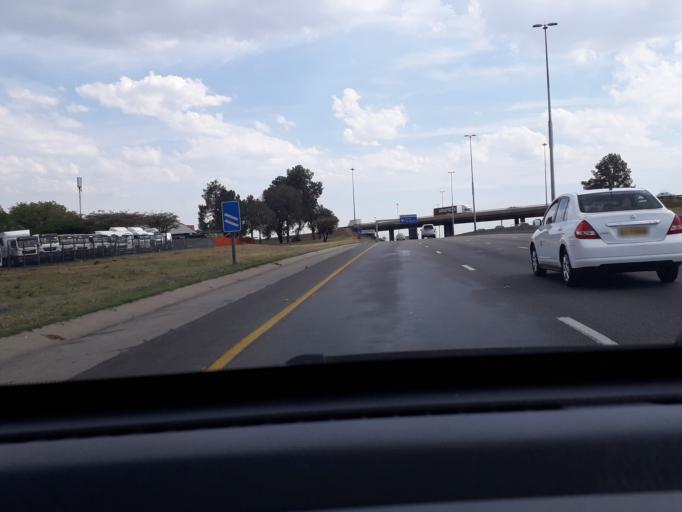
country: ZA
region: Gauteng
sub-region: City of Tshwane Metropolitan Municipality
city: Centurion
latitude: -25.9047
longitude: 28.1599
